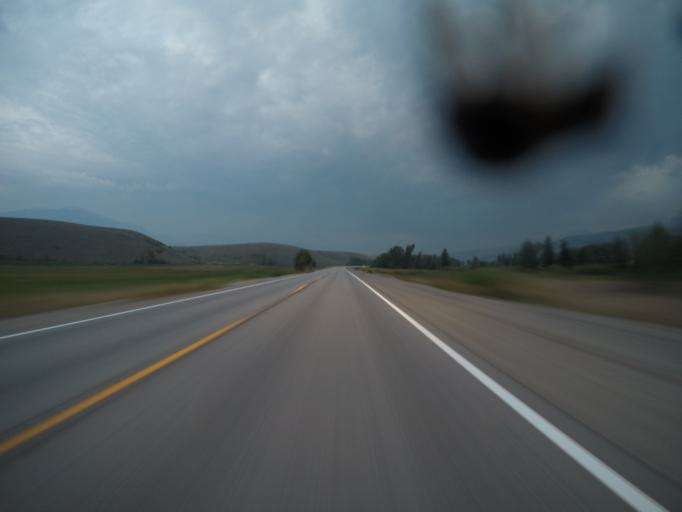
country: US
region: Colorado
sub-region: Summit County
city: Silverthorne
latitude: 39.7927
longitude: -106.1610
